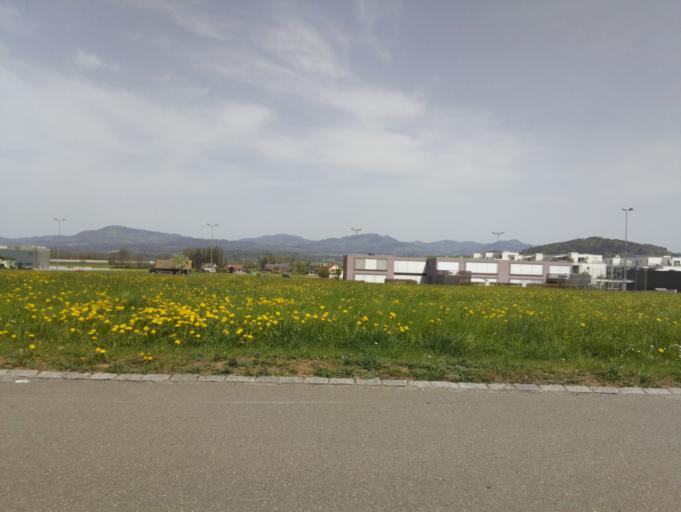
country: CH
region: Schwyz
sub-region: Bezirk March
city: Lachen
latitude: 47.1812
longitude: 8.8699
